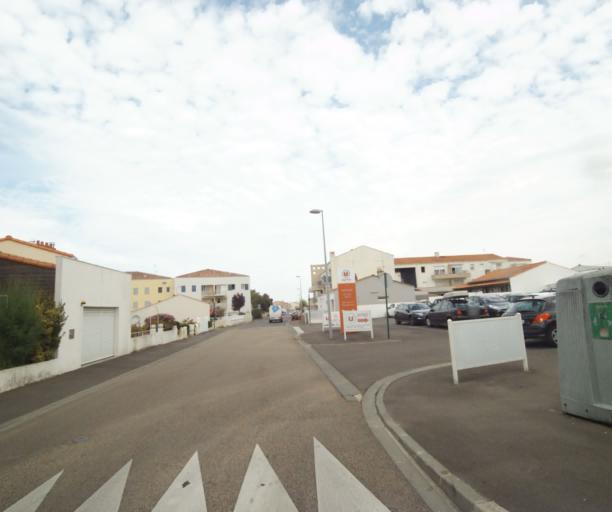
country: FR
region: Pays de la Loire
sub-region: Departement de la Vendee
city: Chateau-d'Olonne
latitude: 46.4936
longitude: -1.7607
